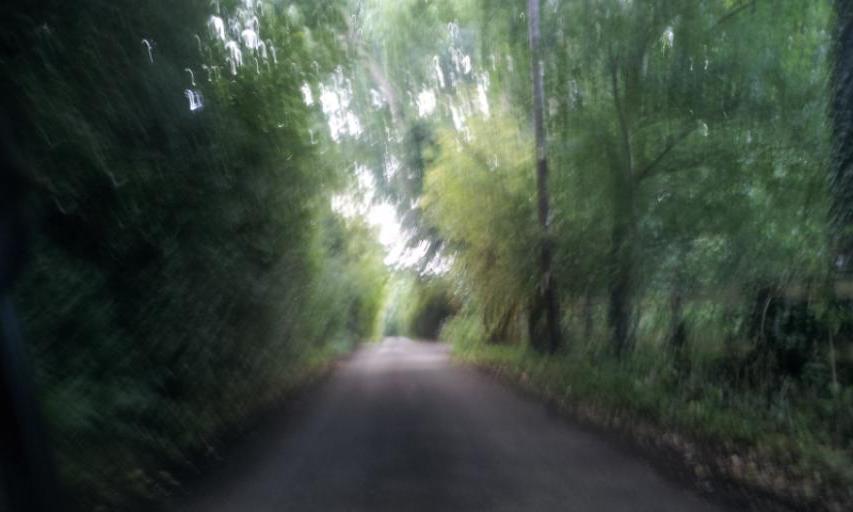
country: GB
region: England
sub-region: Kent
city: Rainham
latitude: 51.3467
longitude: 0.6340
